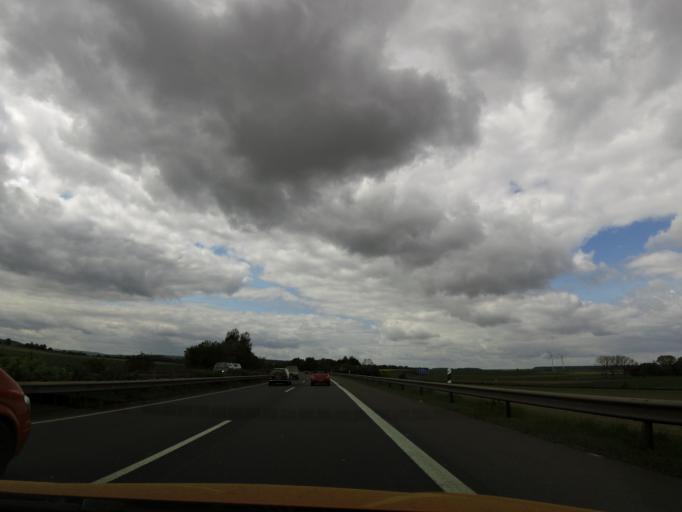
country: DE
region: Lower Saxony
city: Burgdorf
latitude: 52.1375
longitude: 10.2649
